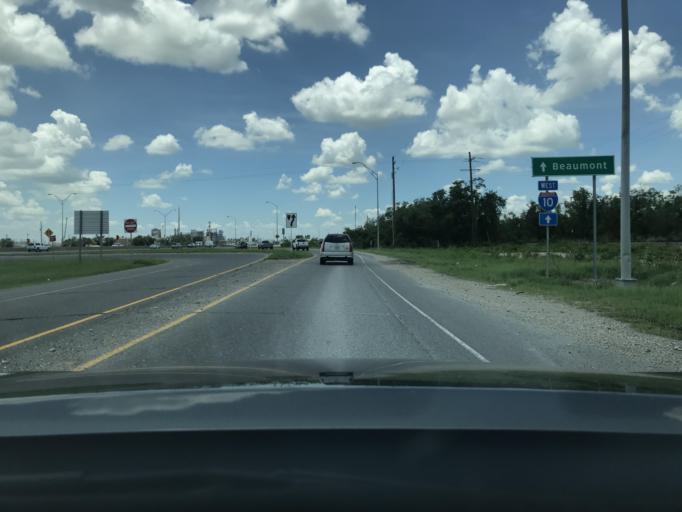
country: US
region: Louisiana
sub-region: Calcasieu Parish
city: Westlake
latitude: 30.2377
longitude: -93.2614
